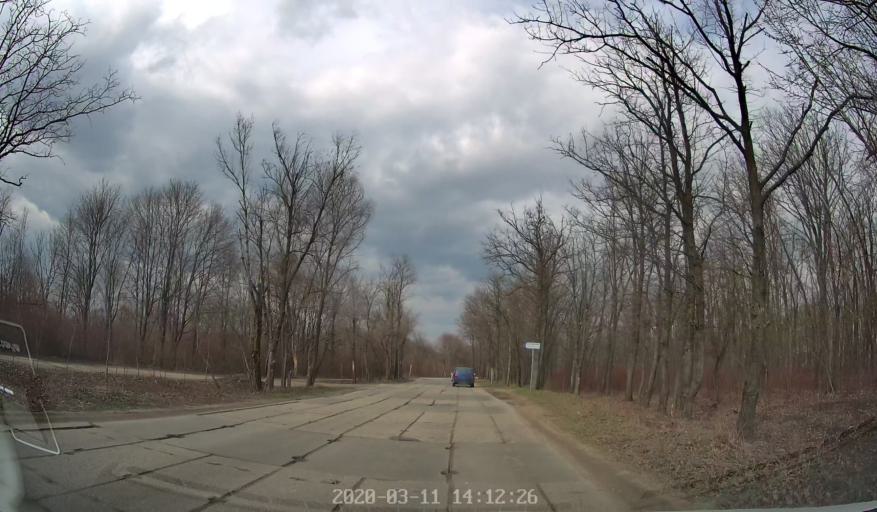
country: MD
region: Chisinau
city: Stauceni
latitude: 47.0529
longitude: 28.8836
